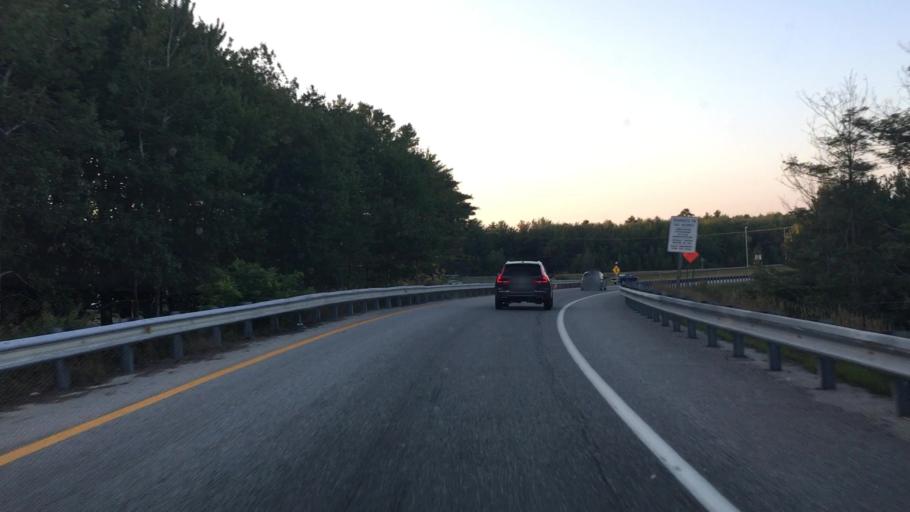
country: US
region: Maine
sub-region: Sagadahoc County
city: Topsham
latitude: 43.9416
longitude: -69.9774
